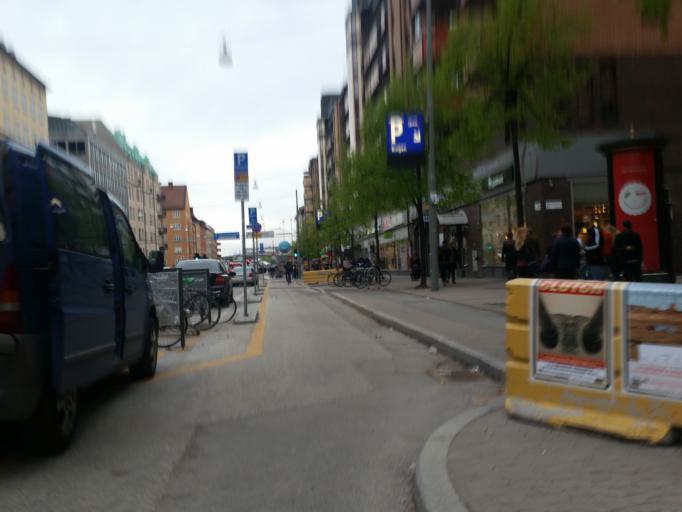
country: SE
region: Stockholm
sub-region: Stockholms Kommun
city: Stockholm
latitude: 59.3094
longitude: 18.0756
